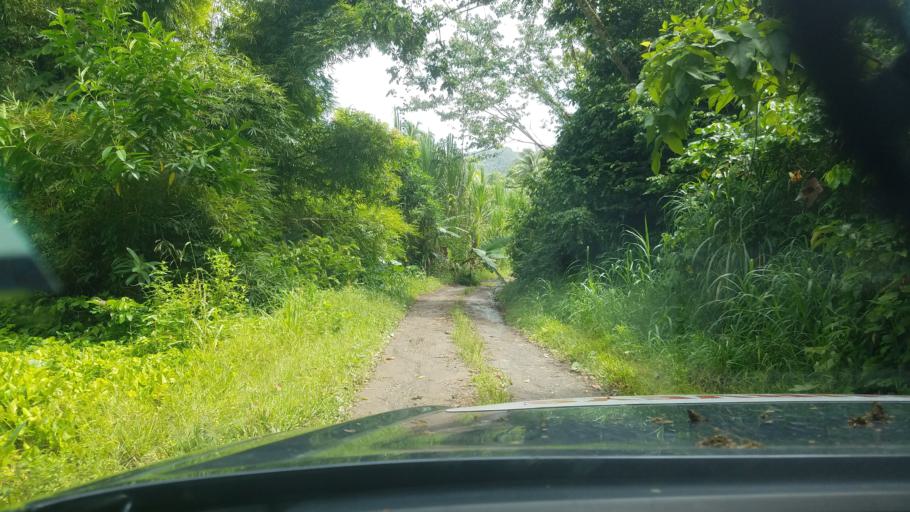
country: LC
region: Anse-la-Raye
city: Anse La Raye
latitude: 13.9401
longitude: -60.9901
